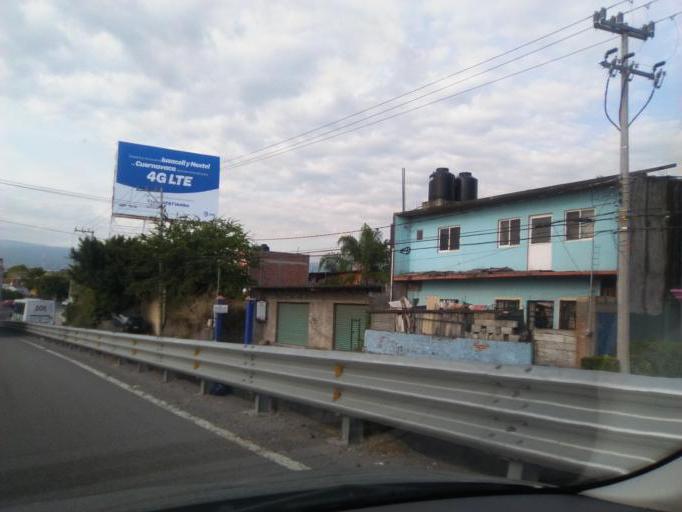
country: MX
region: Morelos
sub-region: Emiliano Zapata
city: Tres de Mayo
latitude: 18.8940
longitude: -99.2268
